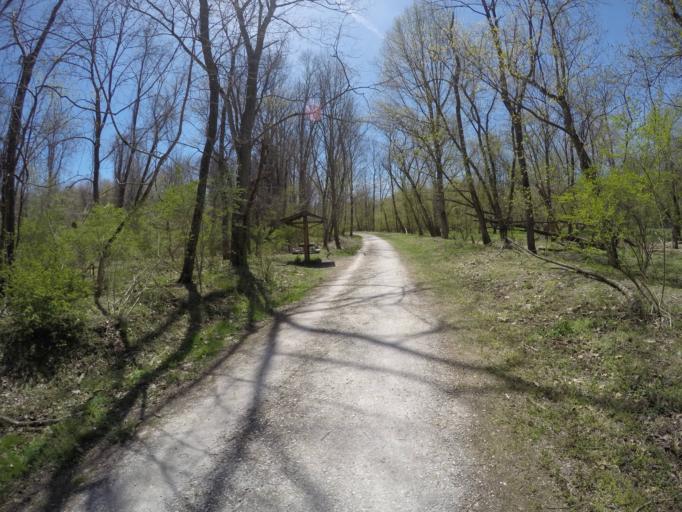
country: US
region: Maryland
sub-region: Baltimore County
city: Hunt Valley
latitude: 39.5452
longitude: -76.6389
